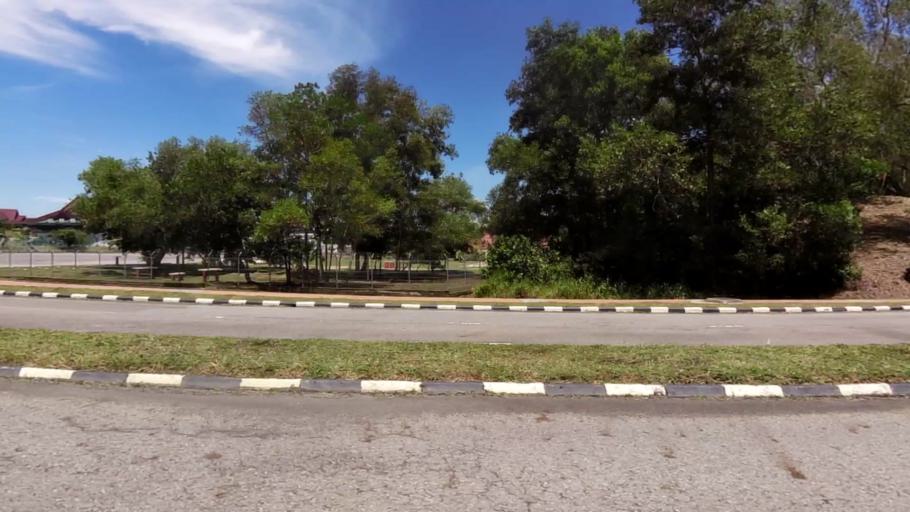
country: BN
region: Brunei and Muara
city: Bandar Seri Begawan
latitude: 4.9297
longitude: 114.9522
